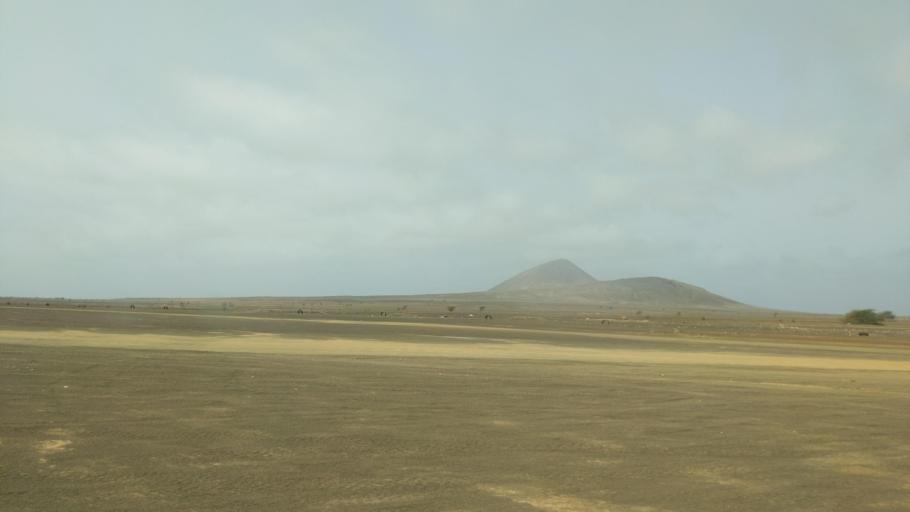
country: CV
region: Sal
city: Espargos
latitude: 16.7953
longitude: -22.9523
